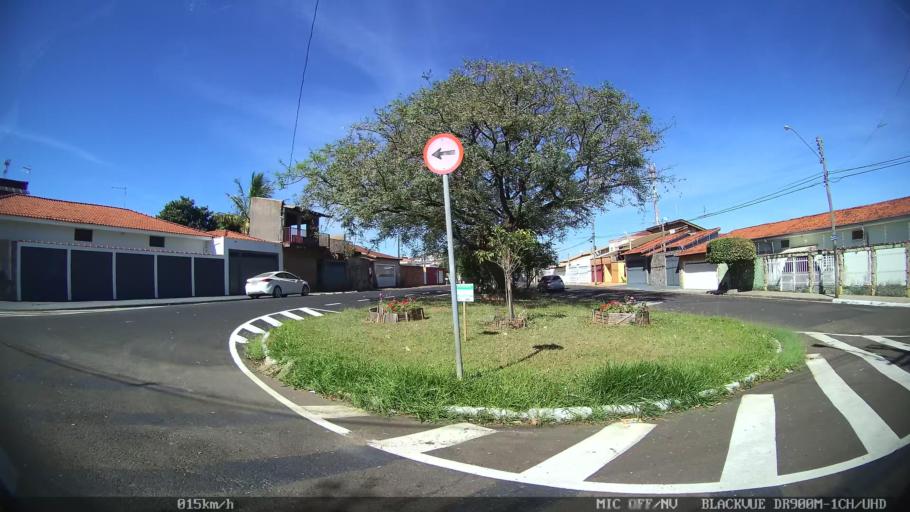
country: BR
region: Sao Paulo
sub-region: Franca
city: Franca
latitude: -20.5440
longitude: -47.3893
